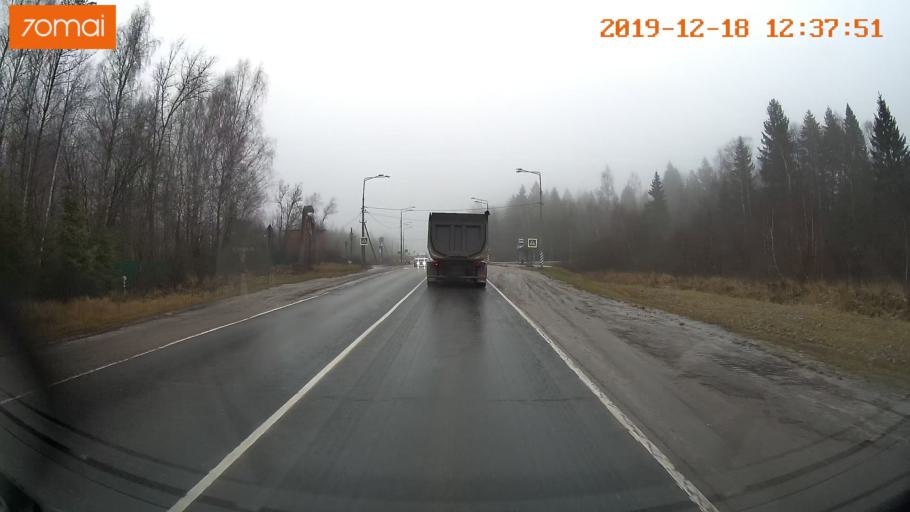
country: RU
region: Moskovskaya
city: Vysokovsk
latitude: 56.1467
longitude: 36.6023
